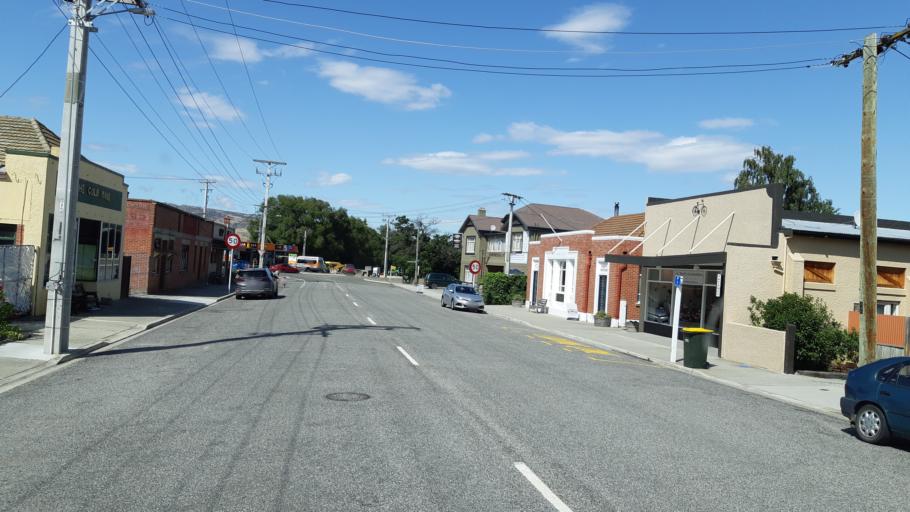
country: NZ
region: Otago
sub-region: Queenstown-Lakes District
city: Wanaka
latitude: -45.0933
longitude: 169.6019
